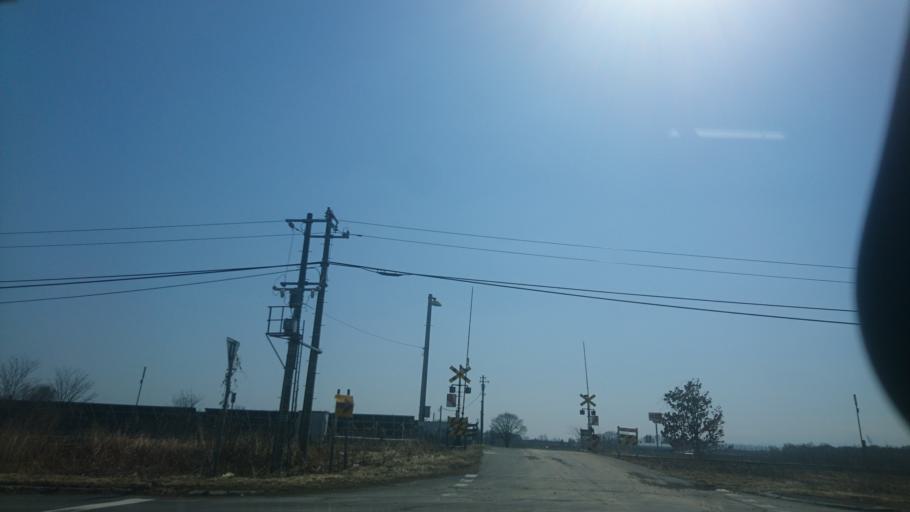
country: JP
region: Hokkaido
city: Obihiro
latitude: 42.9221
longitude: 143.0961
